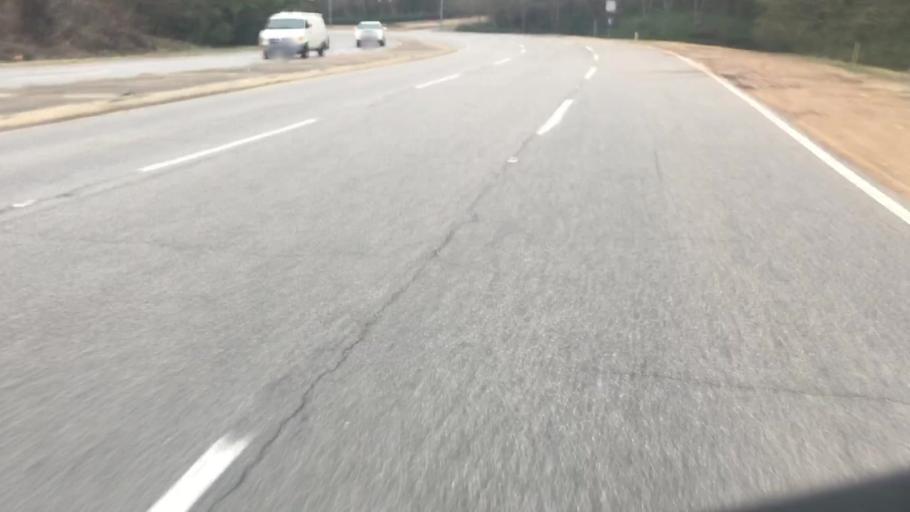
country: US
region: Alabama
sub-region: Jefferson County
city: Vestavia Hills
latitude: 33.4120
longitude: -86.7574
